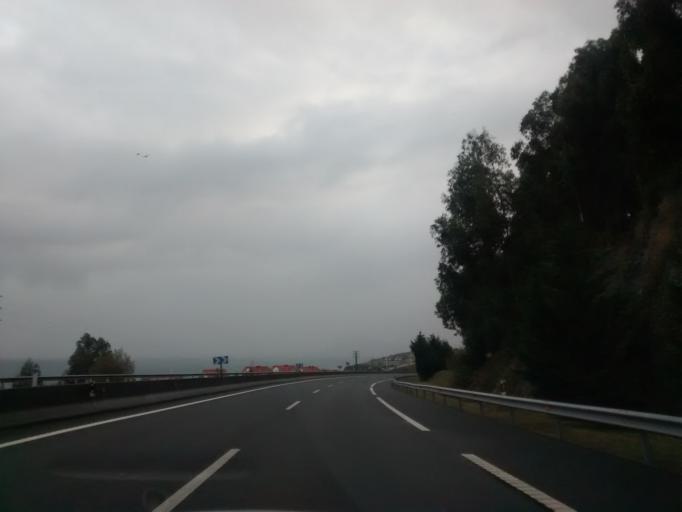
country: ES
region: Cantabria
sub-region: Provincia de Cantabria
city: Castro-Urdiales
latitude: 43.3776
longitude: -3.2250
